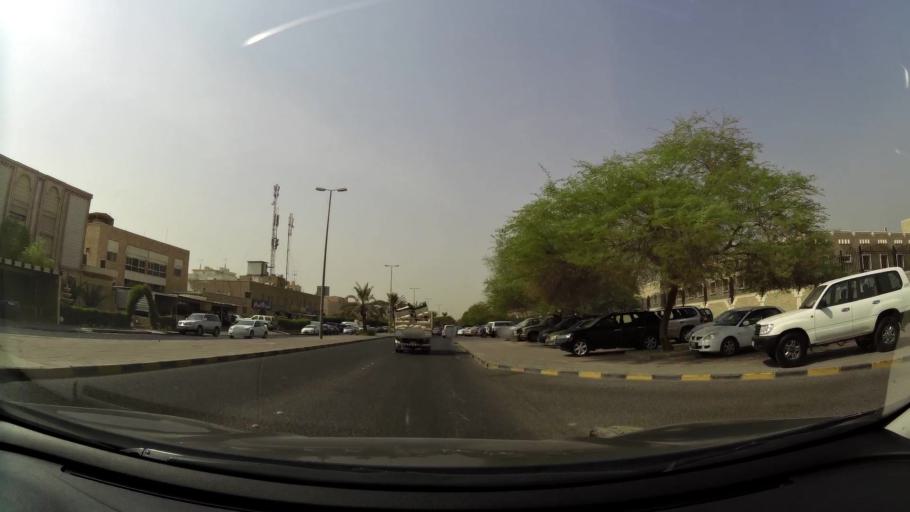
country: KW
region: Al Asimah
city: Ar Rabiyah
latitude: 29.3029
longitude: 47.8713
